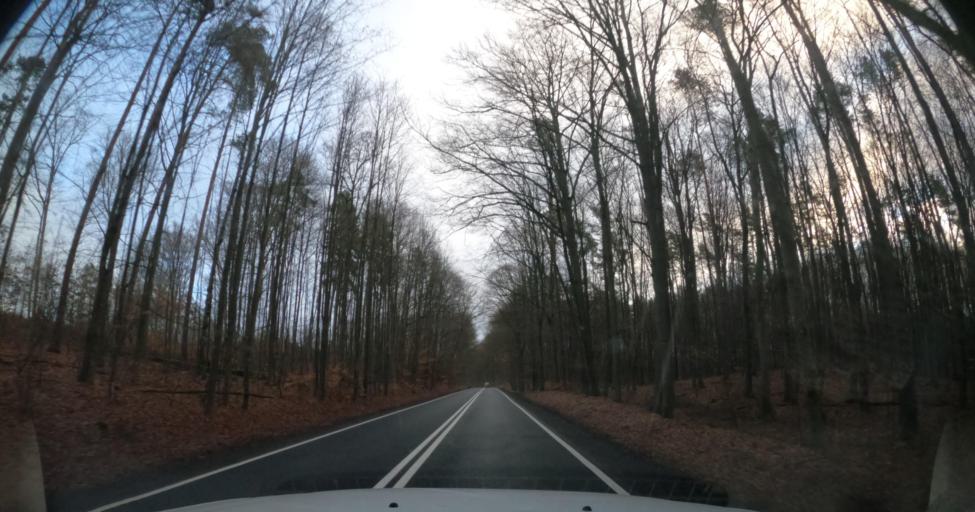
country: PL
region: West Pomeranian Voivodeship
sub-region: Powiat drawski
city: Wierzchowo
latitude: 53.5422
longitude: 16.1070
